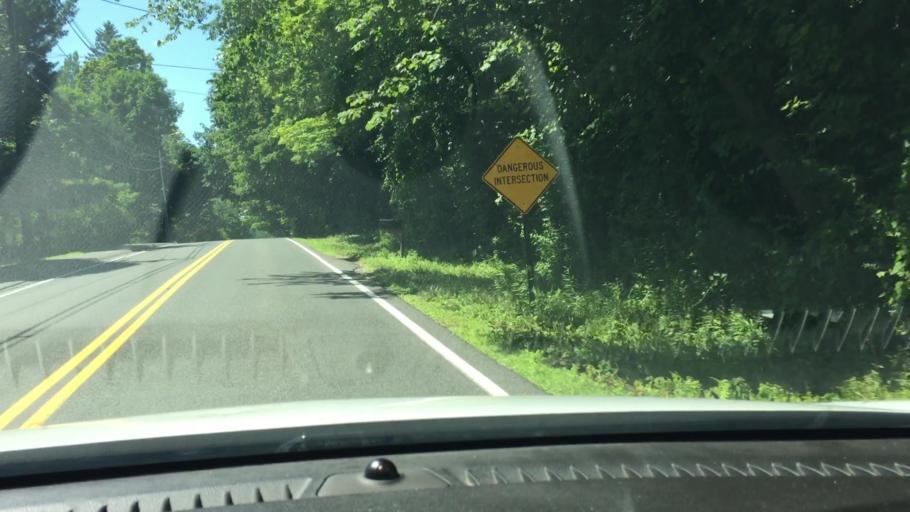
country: US
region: Massachusetts
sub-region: Berkshire County
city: Lenox
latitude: 42.3590
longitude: -73.2596
